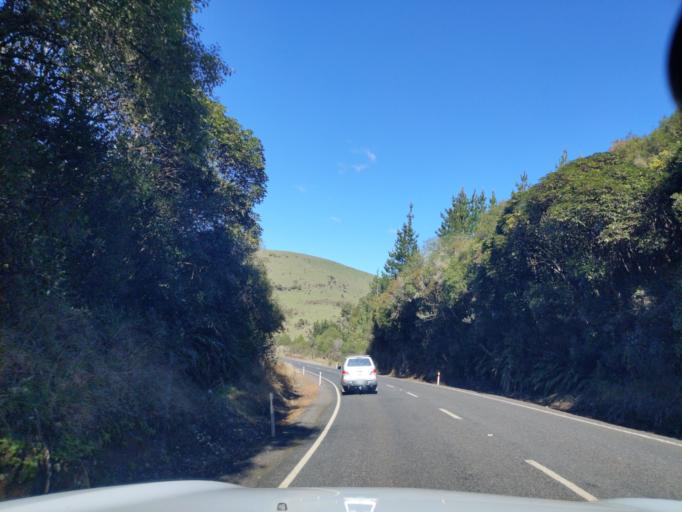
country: NZ
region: Waikato
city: Turangi
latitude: -38.7534
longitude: 175.6751
